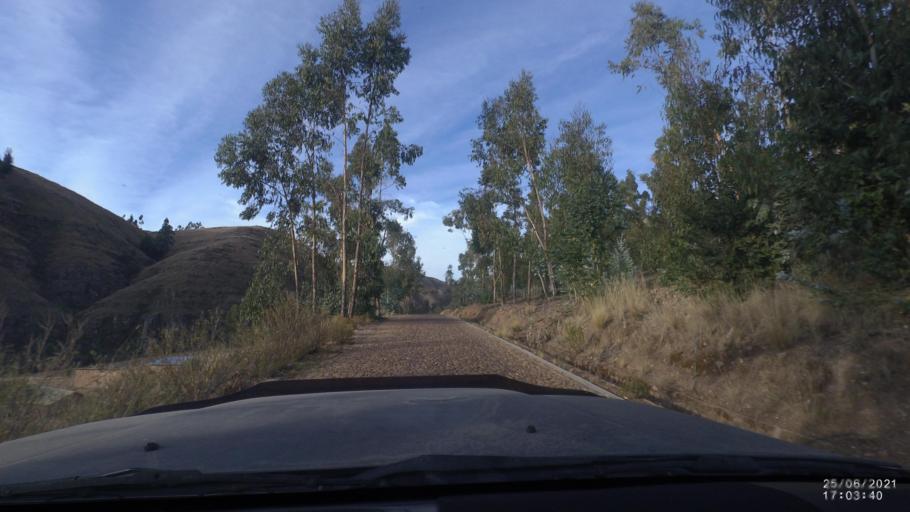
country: BO
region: Cochabamba
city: Arani
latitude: -17.8343
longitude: -65.7272
